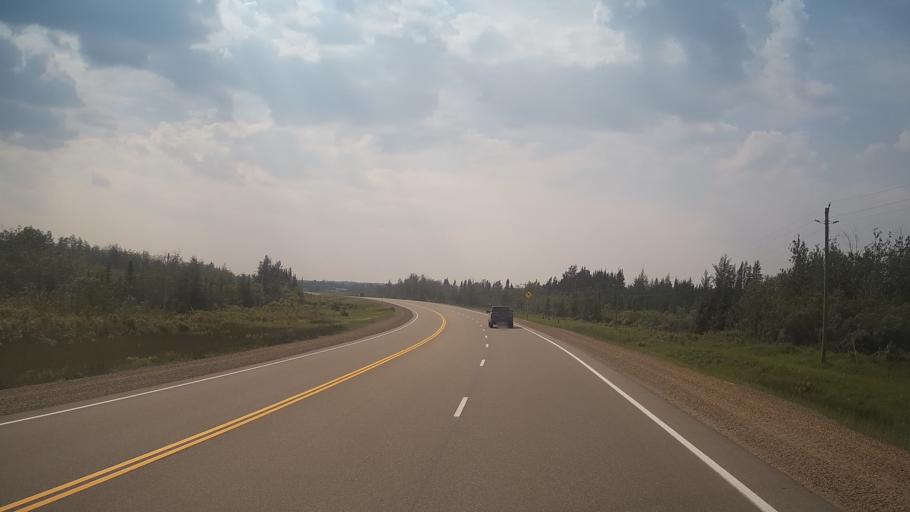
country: CA
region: Ontario
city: Kapuskasing
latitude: 49.4597
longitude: -82.5784
